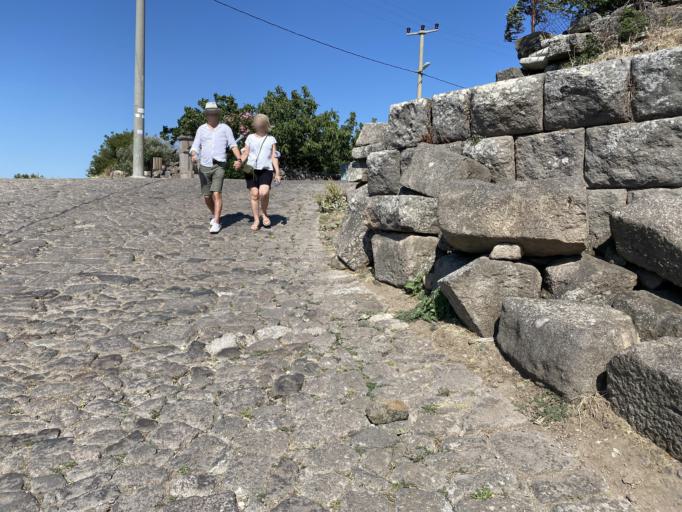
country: TR
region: Canakkale
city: Behram
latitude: 39.4932
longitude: 26.3326
